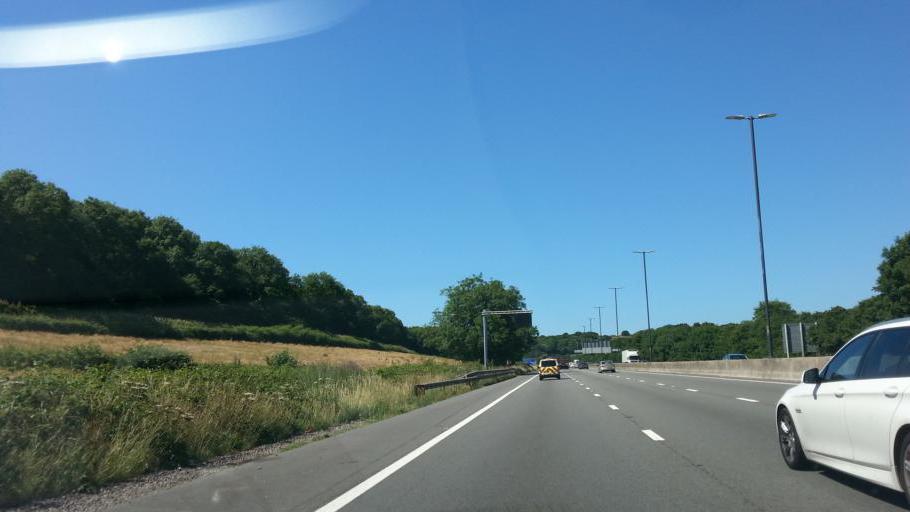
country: GB
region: Wales
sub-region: Newport
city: Newport
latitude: 51.5953
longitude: -3.0199
